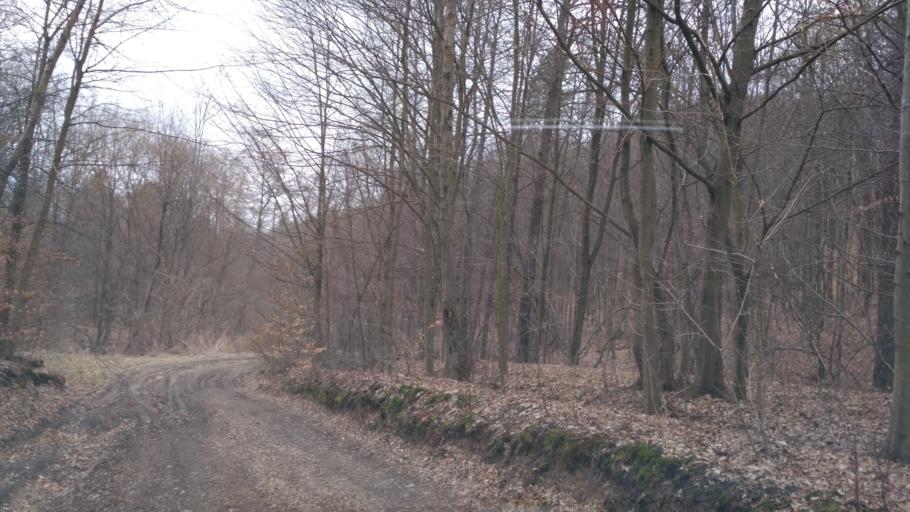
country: SK
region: Presovsky
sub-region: Okres Presov
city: Presov
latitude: 48.9681
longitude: 21.1037
